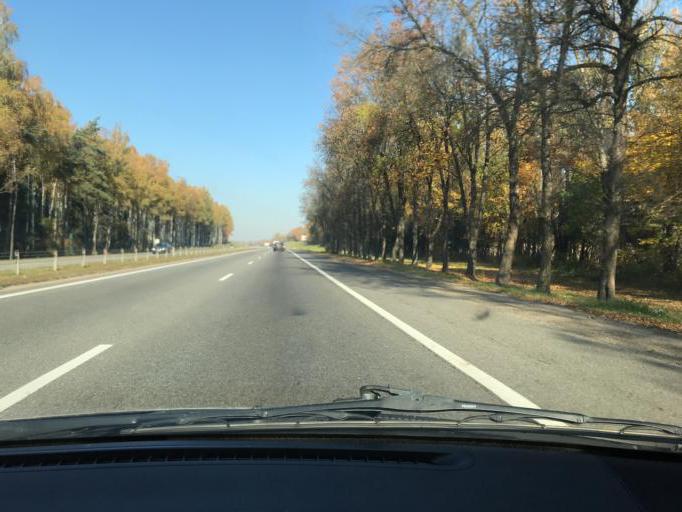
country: BY
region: Minsk
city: Samakhvalavichy
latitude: 53.7614
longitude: 27.5187
